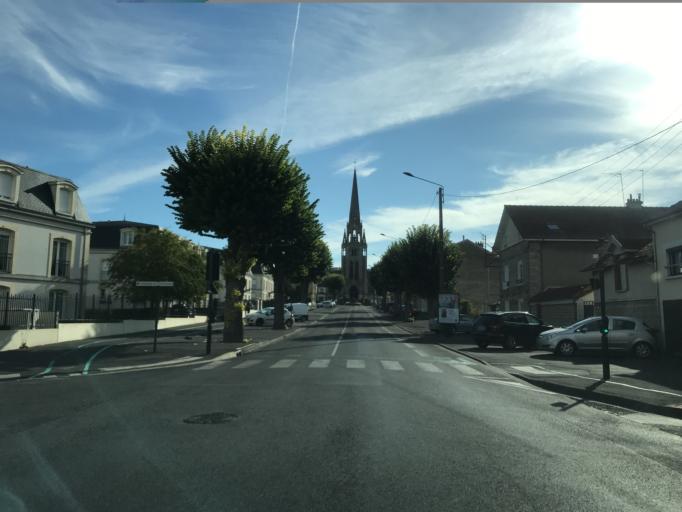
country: FR
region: Champagne-Ardenne
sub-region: Departement de la Marne
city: Pierry
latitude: 49.0322
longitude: 3.9506
